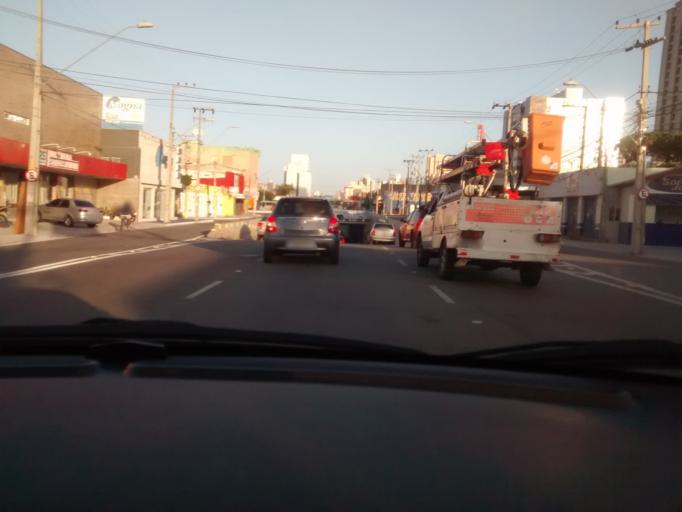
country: BR
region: Ceara
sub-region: Fortaleza
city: Fortaleza
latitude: -3.7394
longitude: -38.4887
